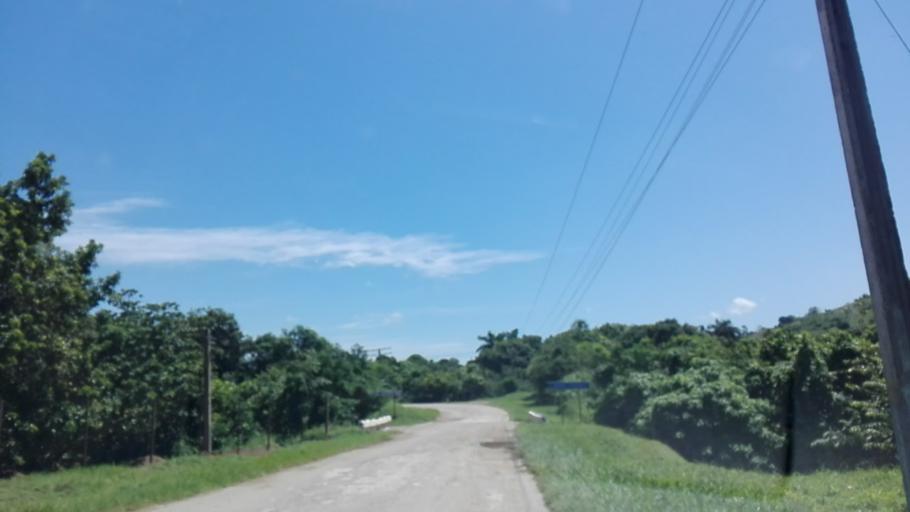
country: CU
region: Granma
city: Bartolome Maso
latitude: 20.1466
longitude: -76.9465
